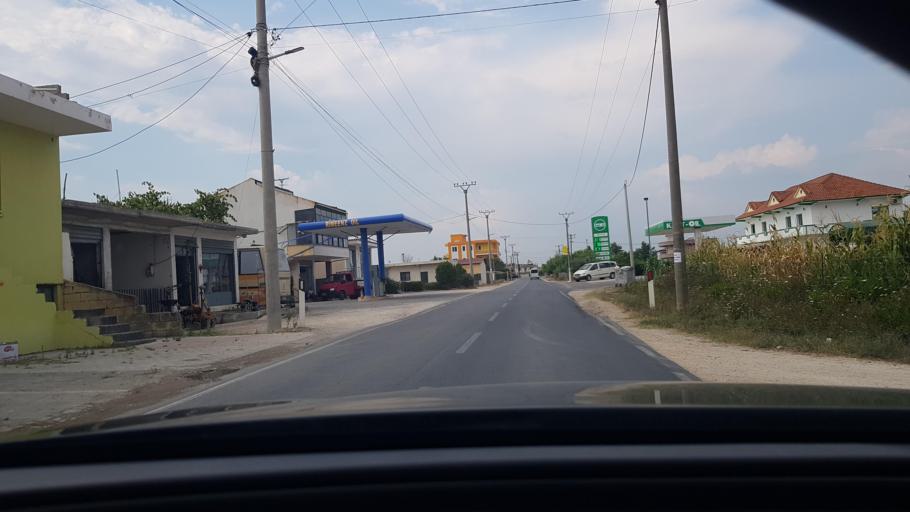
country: AL
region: Durres
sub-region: Rrethi i Durresit
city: Katundi i Ri
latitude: 41.4241
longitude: 19.5482
